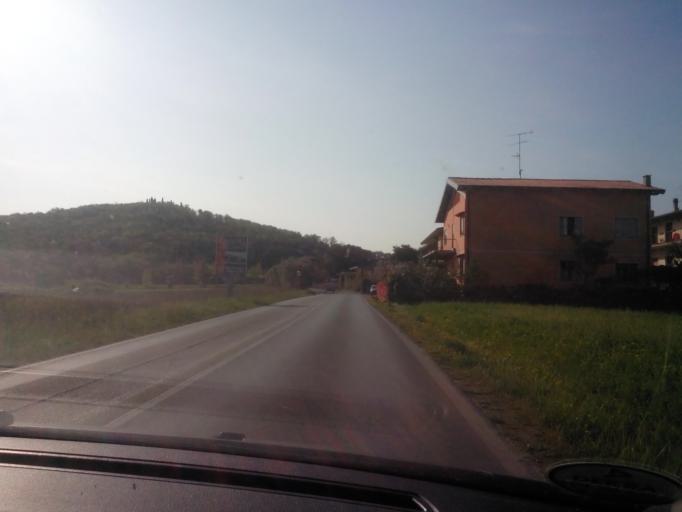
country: IT
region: Lombardy
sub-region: Provincia di Brescia
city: Padenghe sul Garda
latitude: 45.4884
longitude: 10.5153
